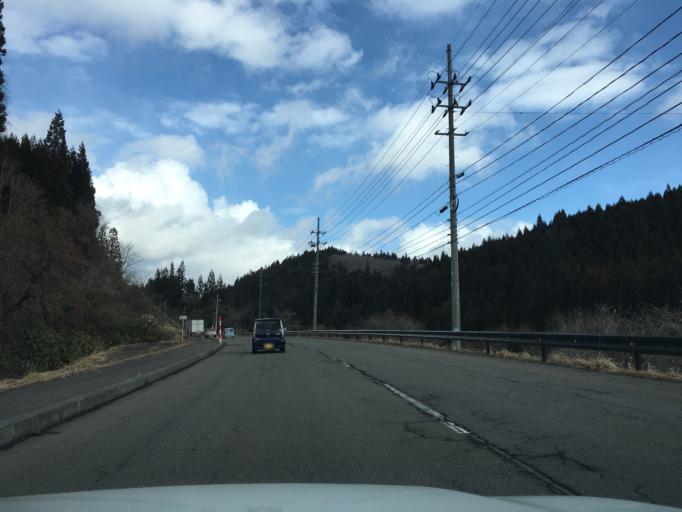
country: JP
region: Akita
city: Takanosu
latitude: 40.0933
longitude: 140.3404
